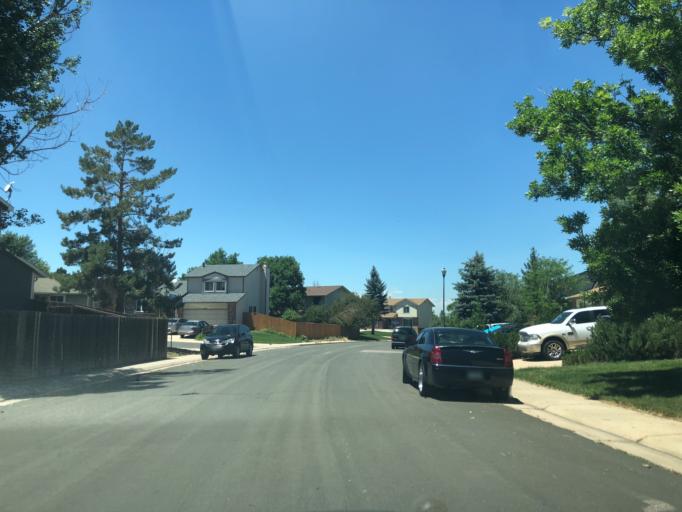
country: US
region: Colorado
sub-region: Arapahoe County
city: Dove Valley
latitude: 39.6173
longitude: -104.7765
